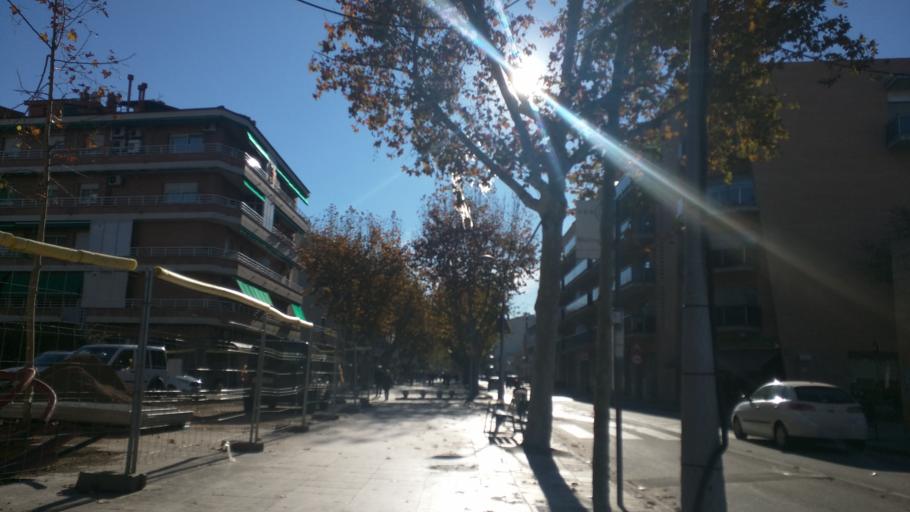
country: ES
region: Catalonia
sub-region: Provincia de Barcelona
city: Molins de Rei
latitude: 41.4129
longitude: 2.0145
